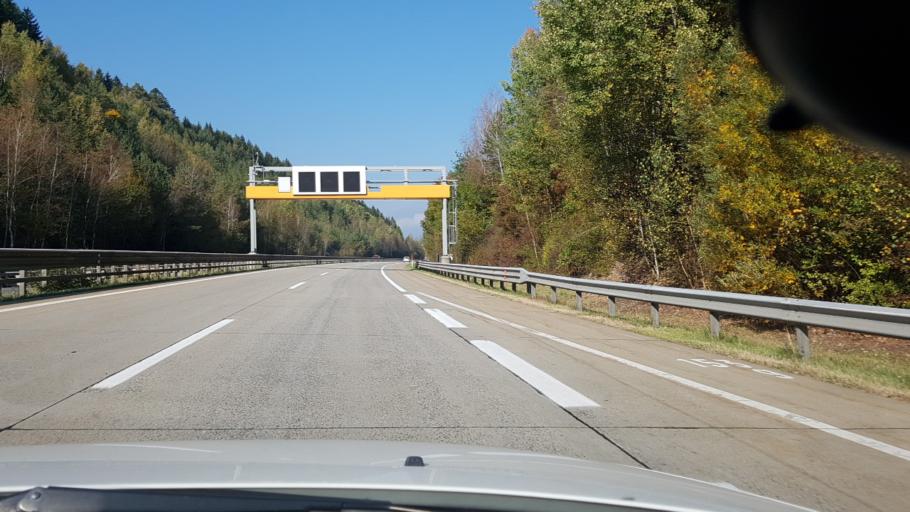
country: AT
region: Carinthia
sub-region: Politischer Bezirk Villach Land
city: Ferndorf
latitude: 46.7334
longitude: 13.5980
